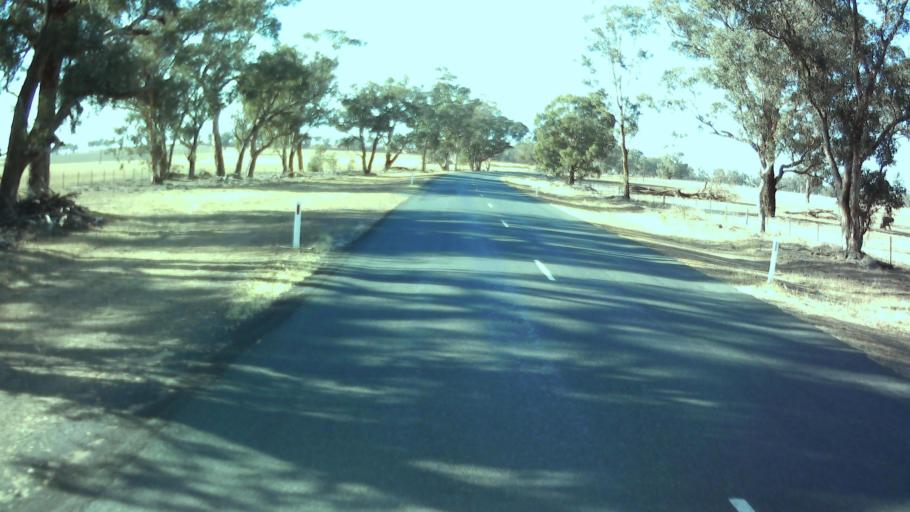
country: AU
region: New South Wales
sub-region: Weddin
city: Grenfell
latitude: -33.9334
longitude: 148.1377
